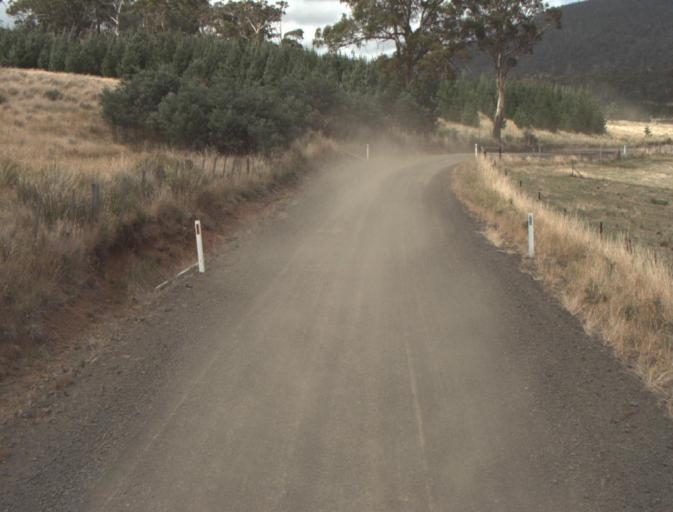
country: AU
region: Tasmania
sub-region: Northern Midlands
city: Evandale
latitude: -41.5088
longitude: 147.3810
